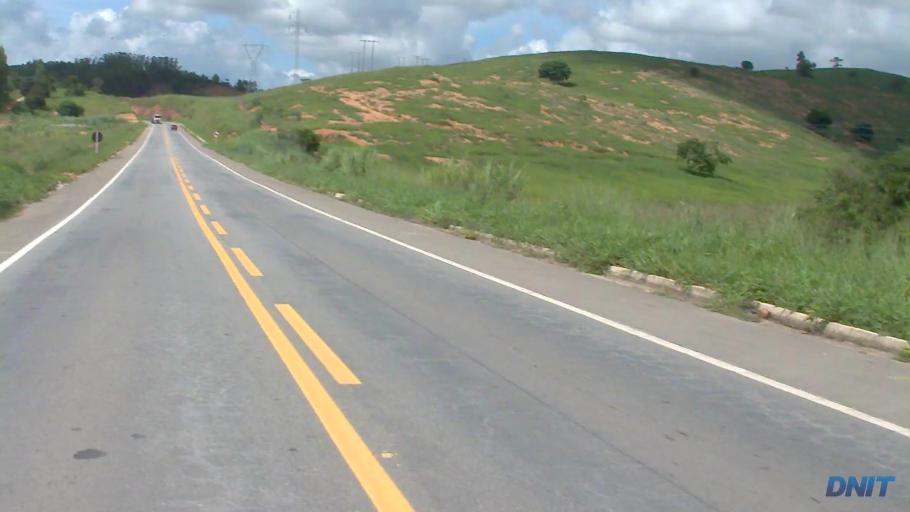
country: BR
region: Minas Gerais
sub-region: Belo Oriente
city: Belo Oriente
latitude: -19.0912
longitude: -42.1889
